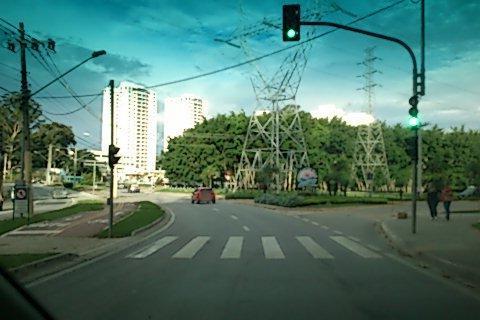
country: BR
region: Sao Paulo
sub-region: Sao Jose Dos Campos
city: Sao Jose dos Campos
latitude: -23.1989
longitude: -45.9149
